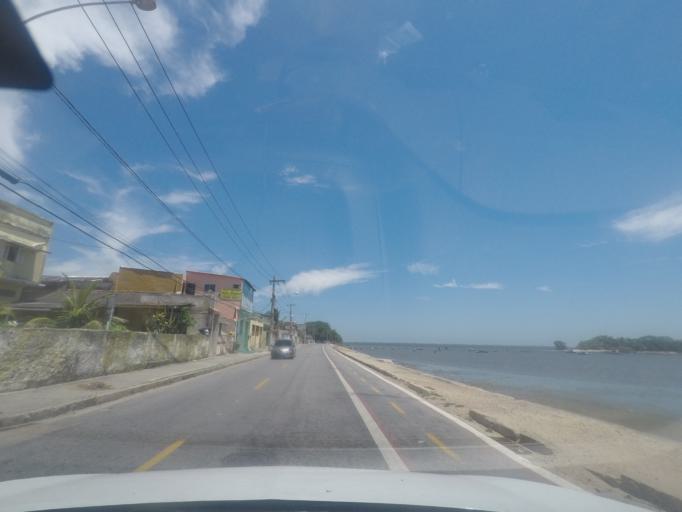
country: BR
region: Rio de Janeiro
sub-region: Itaguai
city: Itaguai
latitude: -22.9815
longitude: -43.7024
